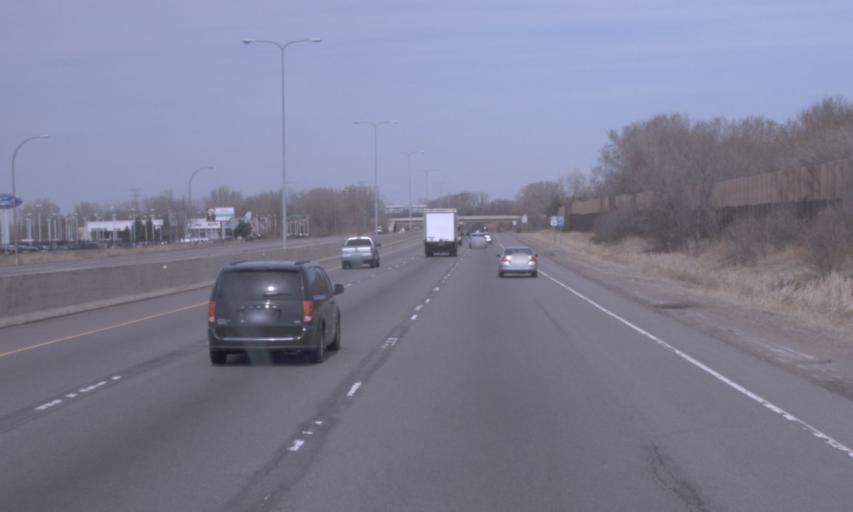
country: US
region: Minnesota
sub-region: Anoka County
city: Coon Rapids
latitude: 45.1576
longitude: -93.2796
